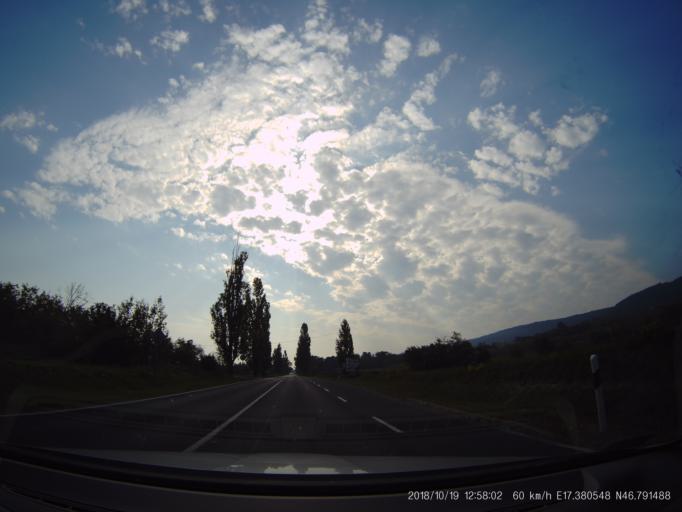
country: HU
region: Zala
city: Vonyarcvashegy
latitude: 46.7914
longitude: 17.3805
